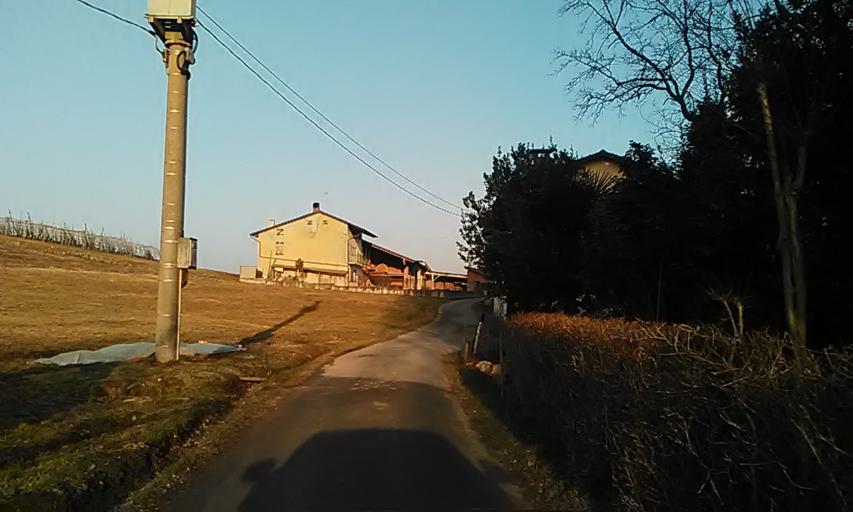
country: IT
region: Piedmont
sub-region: Provincia di Biella
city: Dorzano
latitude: 45.4142
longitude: 8.1172
